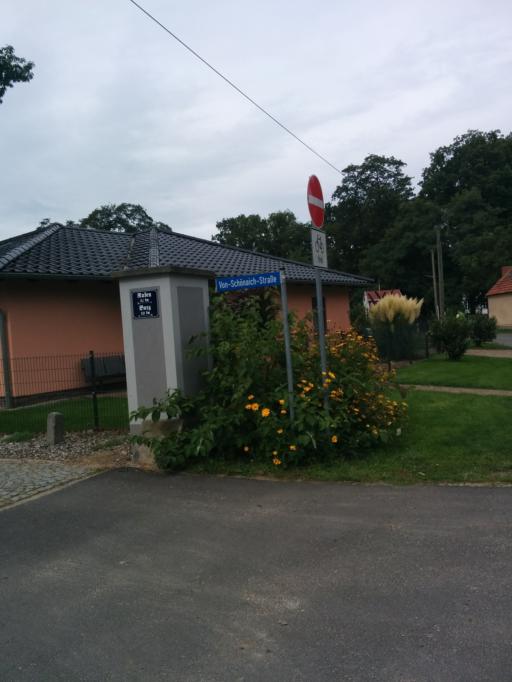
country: DE
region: Brandenburg
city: Werben
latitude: 51.8154
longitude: 14.1841
